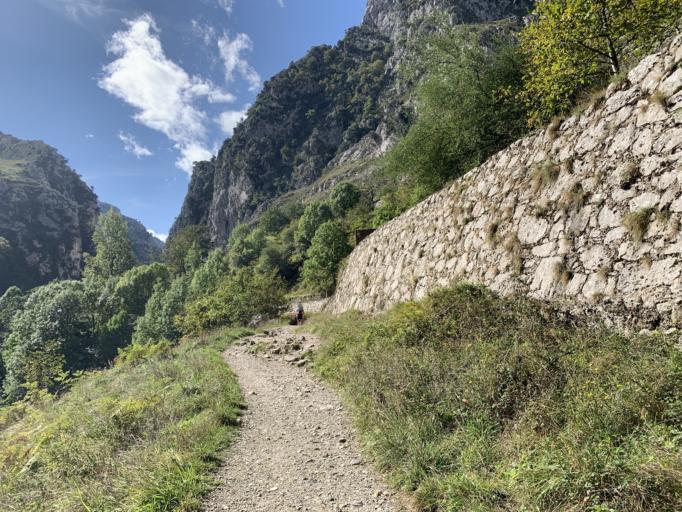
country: ES
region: Asturias
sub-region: Province of Asturias
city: Carrena
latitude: 43.2437
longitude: -4.8895
